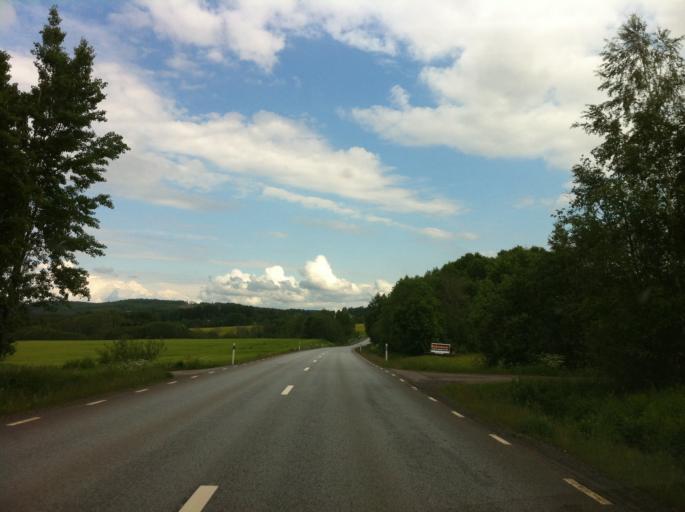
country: SE
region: Vaermland
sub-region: Sunne Kommun
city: Sunne
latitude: 59.7221
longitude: 13.1351
